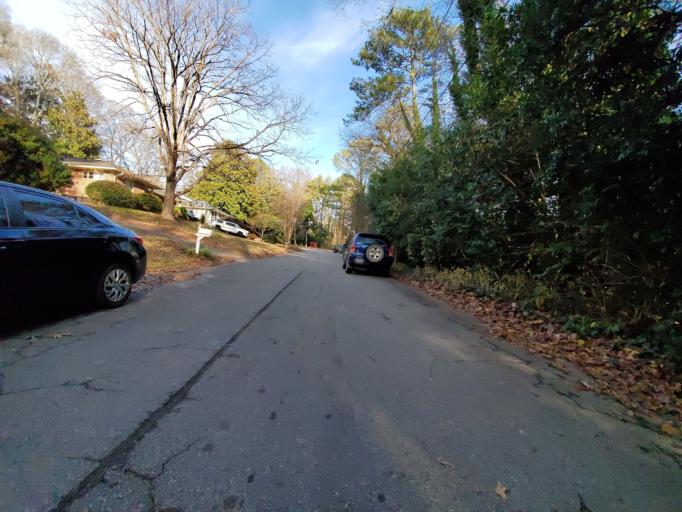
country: US
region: Georgia
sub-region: DeKalb County
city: North Decatur
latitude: 33.7921
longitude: -84.2951
